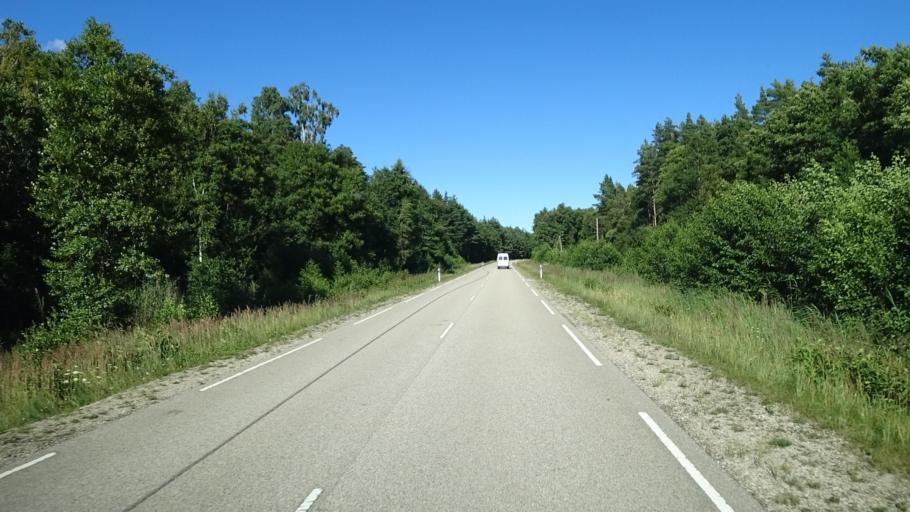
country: LV
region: Dundaga
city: Dundaga
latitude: 57.7374
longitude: 22.5302
